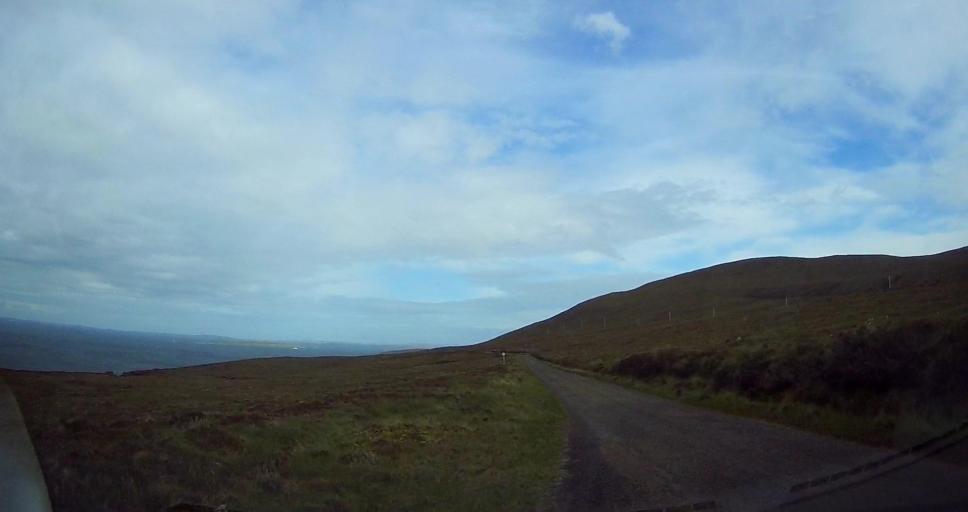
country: GB
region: Scotland
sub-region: Orkney Islands
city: Stromness
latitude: 58.8962
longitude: -3.2724
